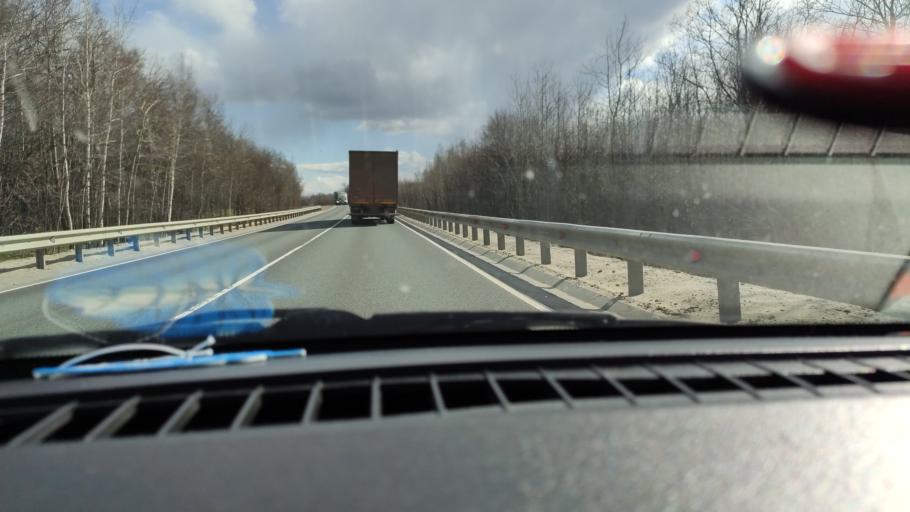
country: RU
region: Saratov
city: Khvalynsk
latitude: 52.4758
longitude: 48.0136
